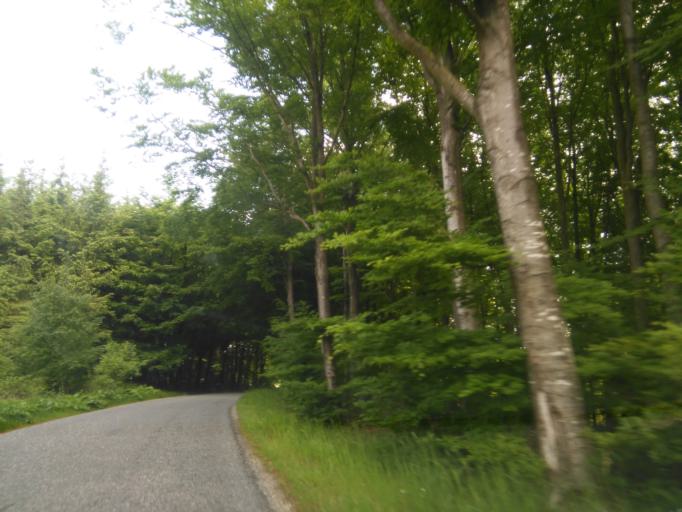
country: DK
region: Central Jutland
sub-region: Favrskov Kommune
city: Hammel
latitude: 56.2314
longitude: 9.9296
